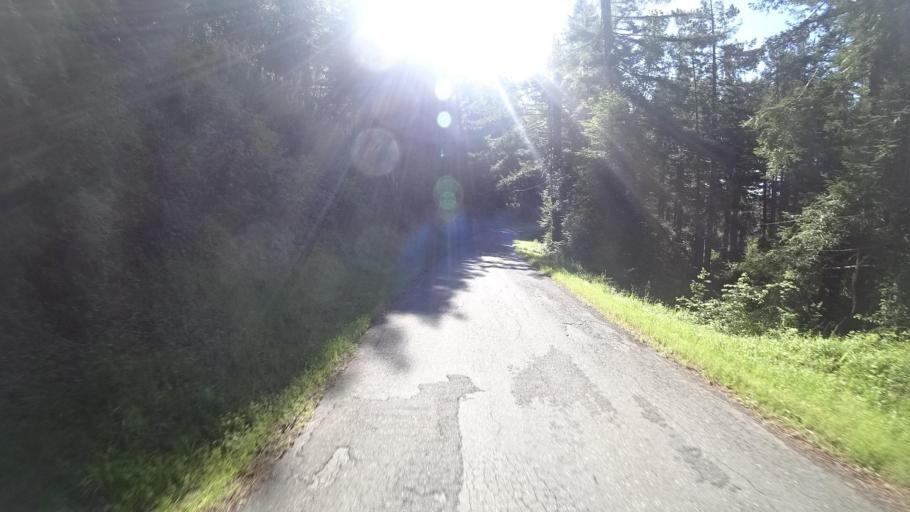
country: US
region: California
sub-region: Humboldt County
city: Rio Dell
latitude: 40.4552
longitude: -123.9912
